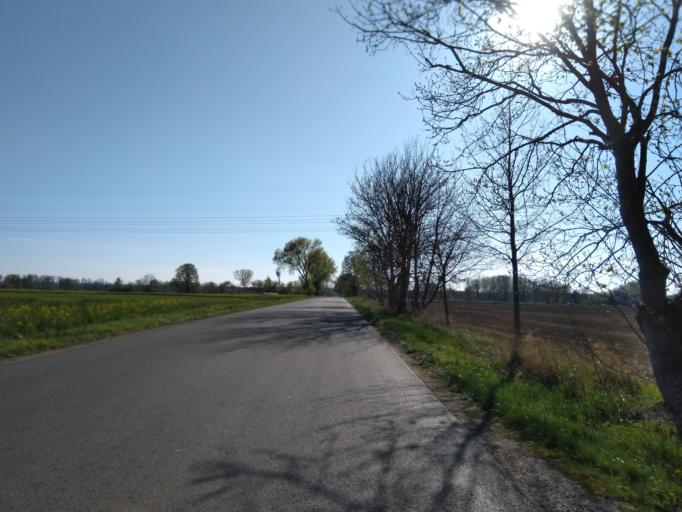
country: DE
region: Brandenburg
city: Bliesdorf
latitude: 52.6981
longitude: 14.1759
